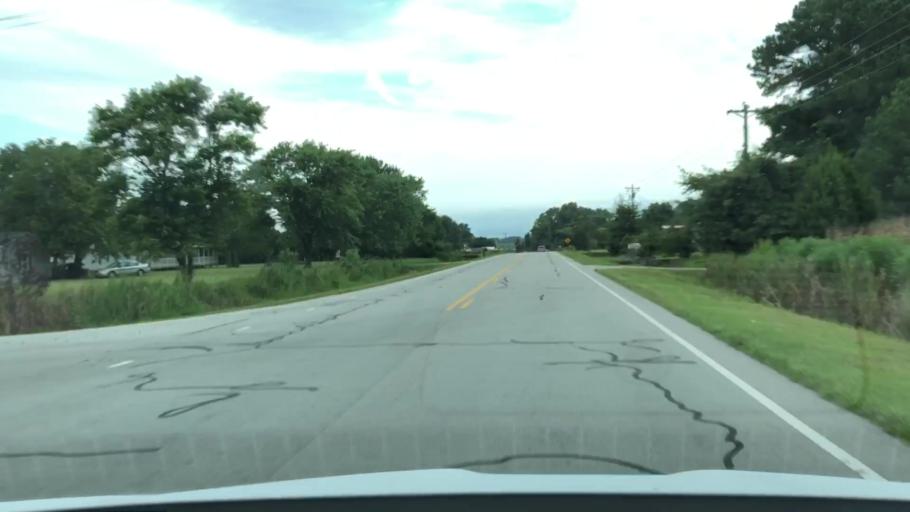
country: US
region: North Carolina
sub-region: Lenoir County
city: Kinston
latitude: 35.1352
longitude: -77.5273
